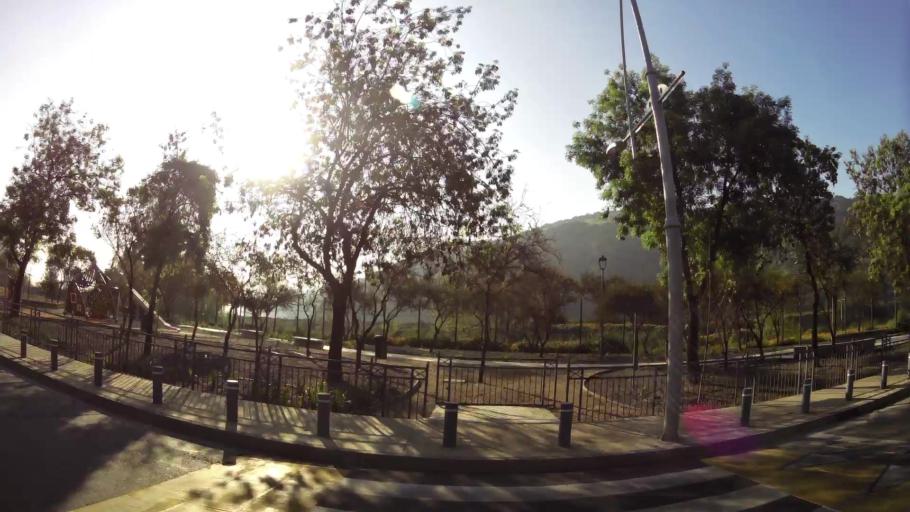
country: CL
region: Santiago Metropolitan
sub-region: Provincia de Santiago
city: Villa Presidente Frei, Nunoa, Santiago, Chile
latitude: -33.3781
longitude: -70.5314
